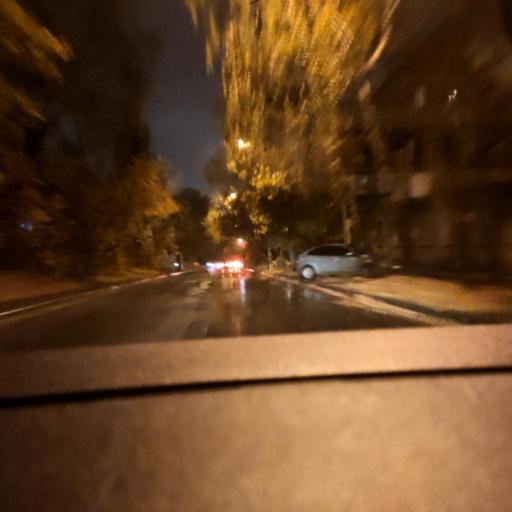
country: RU
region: Voronezj
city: Voronezh
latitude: 51.6783
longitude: 39.1381
